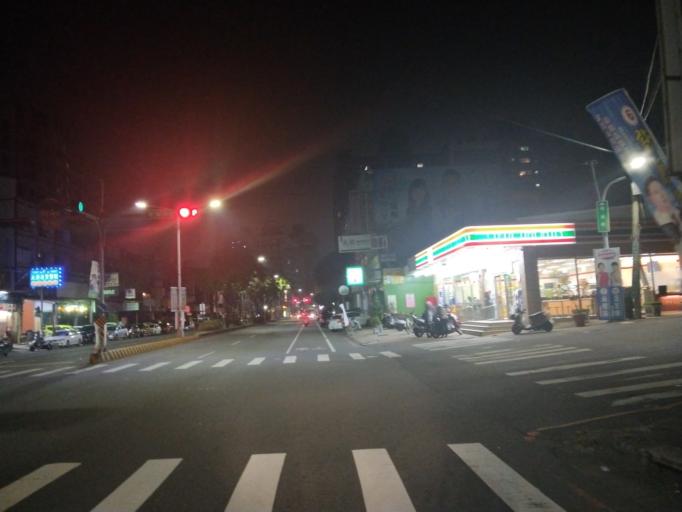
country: TW
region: Taiwan
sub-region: Changhua
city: Chang-hua
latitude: 24.0591
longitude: 120.5347
